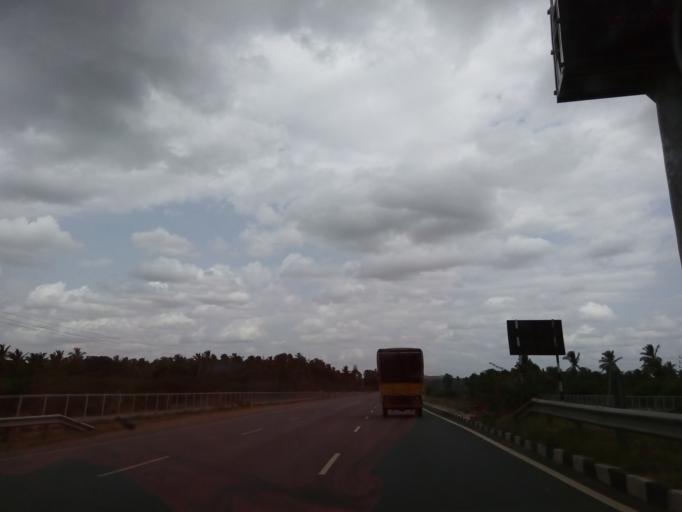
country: IN
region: Karnataka
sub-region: Chitradurga
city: Hiriyur
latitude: 13.9494
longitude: 76.6243
